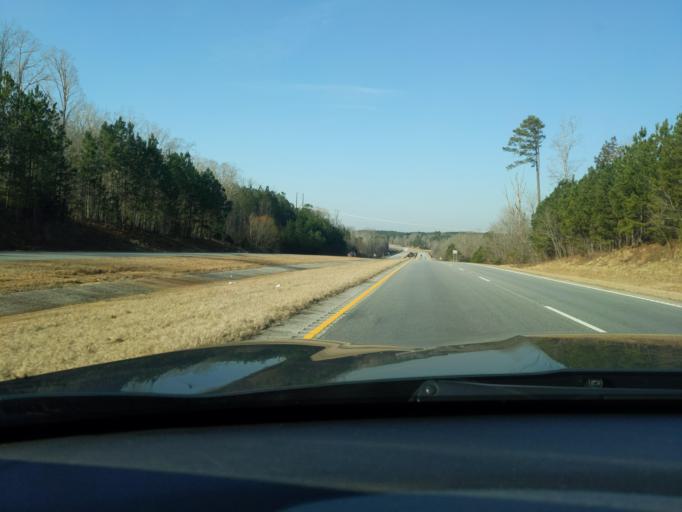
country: US
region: South Carolina
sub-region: Abbeville County
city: Calhoun Falls
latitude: 34.1109
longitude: -82.5044
